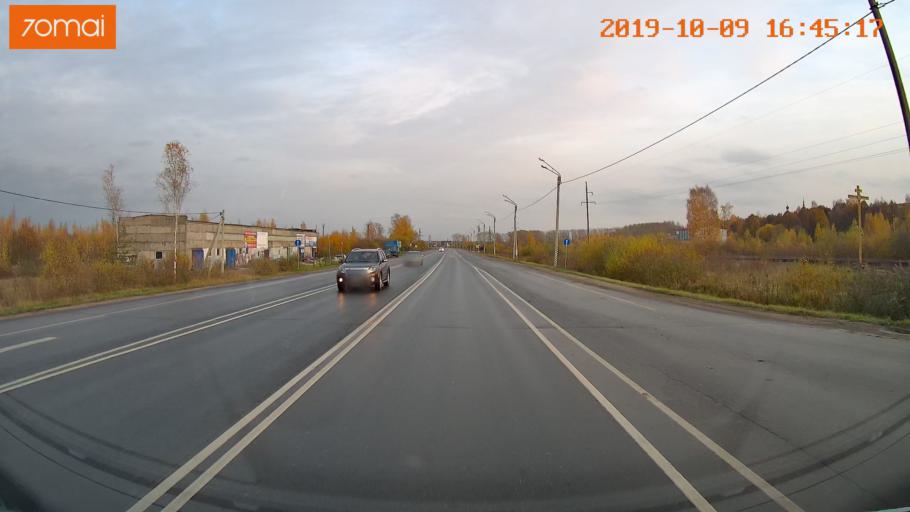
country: RU
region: Kostroma
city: Volgorechensk
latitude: 57.4471
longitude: 41.1526
